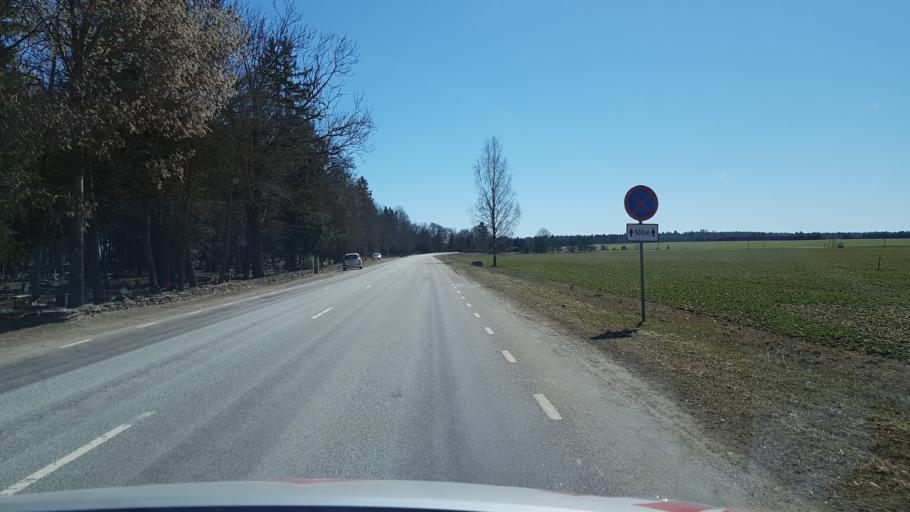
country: EE
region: Laeaene-Virumaa
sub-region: Viru-Nigula vald
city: Kunda
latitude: 59.4396
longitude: 26.6971
